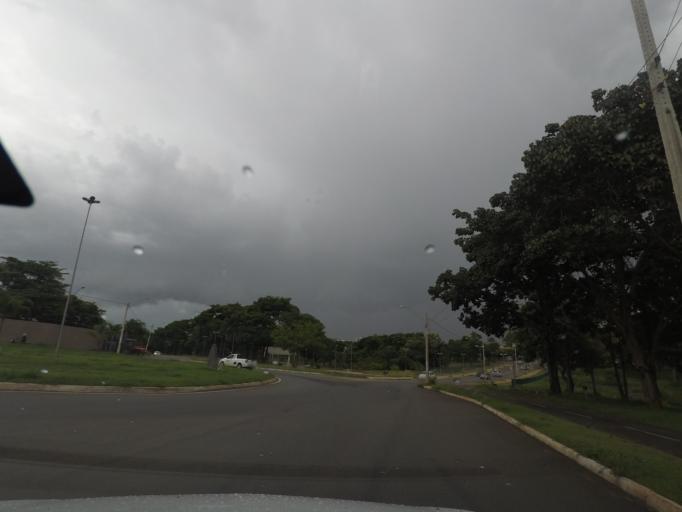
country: BR
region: Goias
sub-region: Goiania
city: Goiania
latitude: -16.7159
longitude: -49.3223
